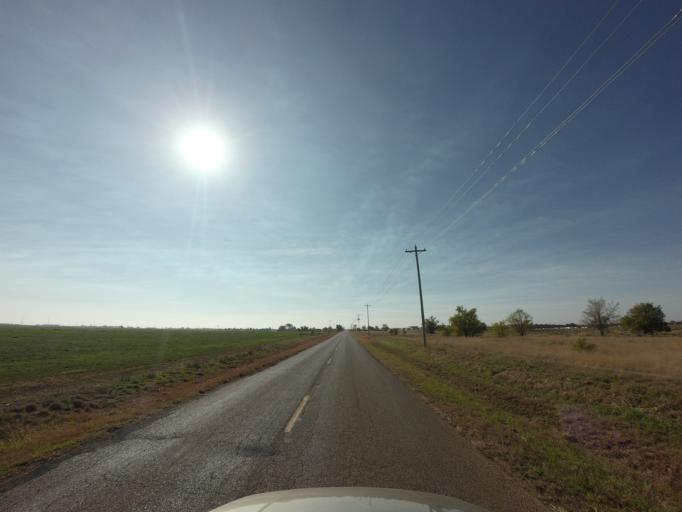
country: US
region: New Mexico
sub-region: Curry County
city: Clovis
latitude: 34.4098
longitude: -103.1611
